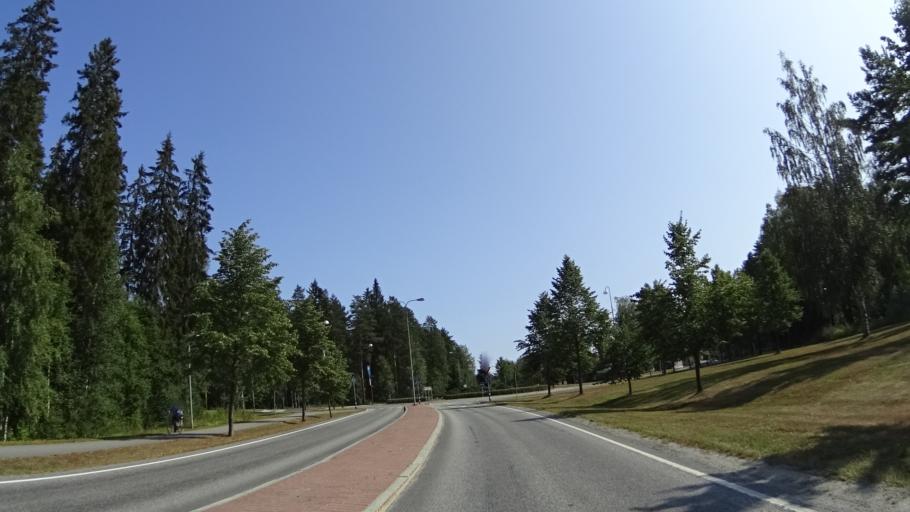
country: FI
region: Pirkanmaa
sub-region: Ylae-Pirkanmaa
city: Maenttae
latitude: 62.0289
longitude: 24.6103
